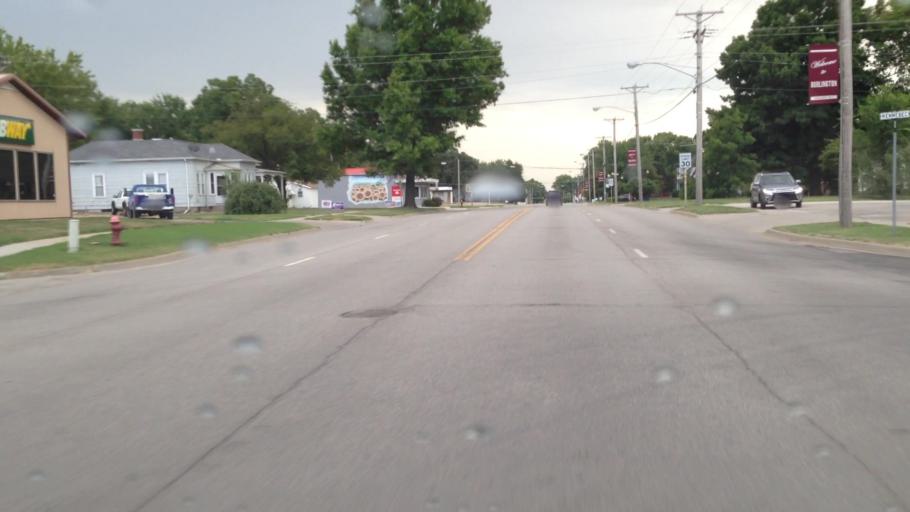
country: US
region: Kansas
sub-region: Coffey County
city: Burlington
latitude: 38.1993
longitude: -95.7385
